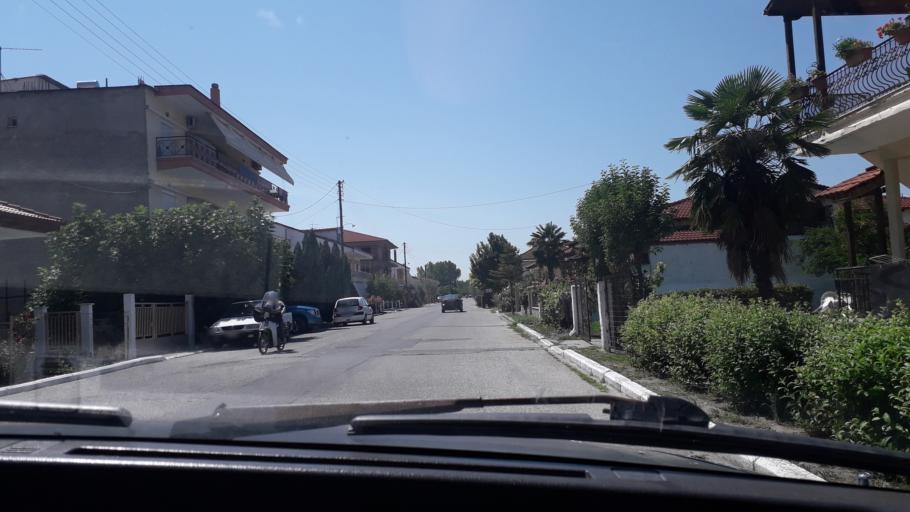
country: GR
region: Central Macedonia
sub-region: Nomos Pellis
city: Aridaia
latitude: 40.9696
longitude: 22.0590
